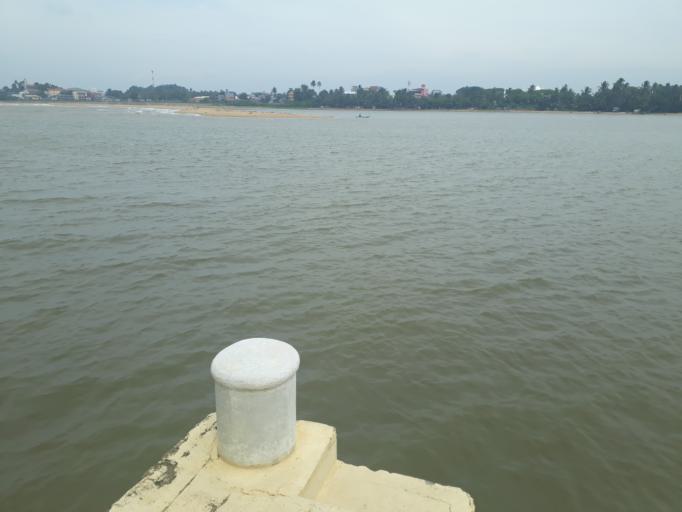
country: LK
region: Western
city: Kalutara
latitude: 6.5683
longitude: 79.9608
